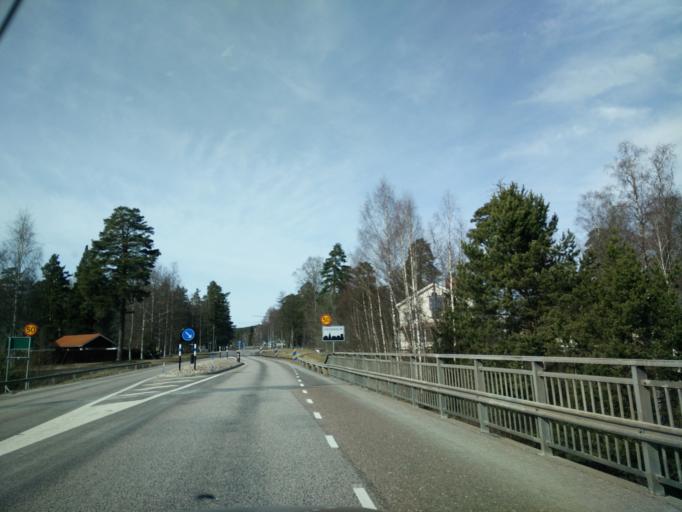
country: SE
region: Vaermland
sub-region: Hagfors Kommun
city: Hagfors
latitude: 60.0201
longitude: 13.6229
